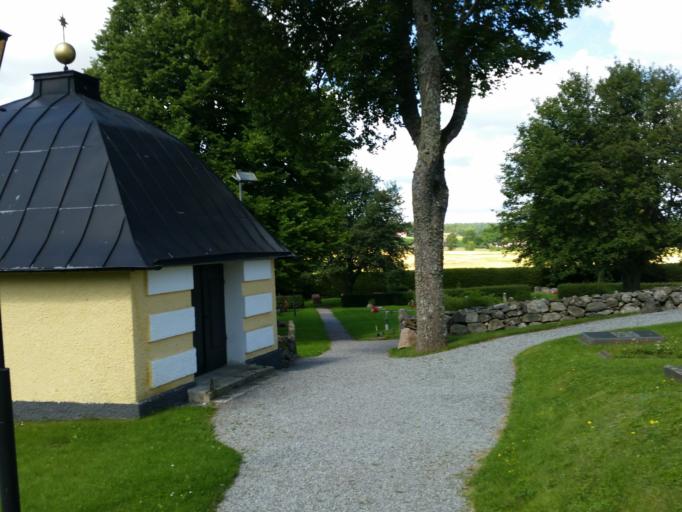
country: SE
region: Soedermanland
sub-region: Trosa Kommun
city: Vagnharad
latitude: 59.0130
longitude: 17.5891
